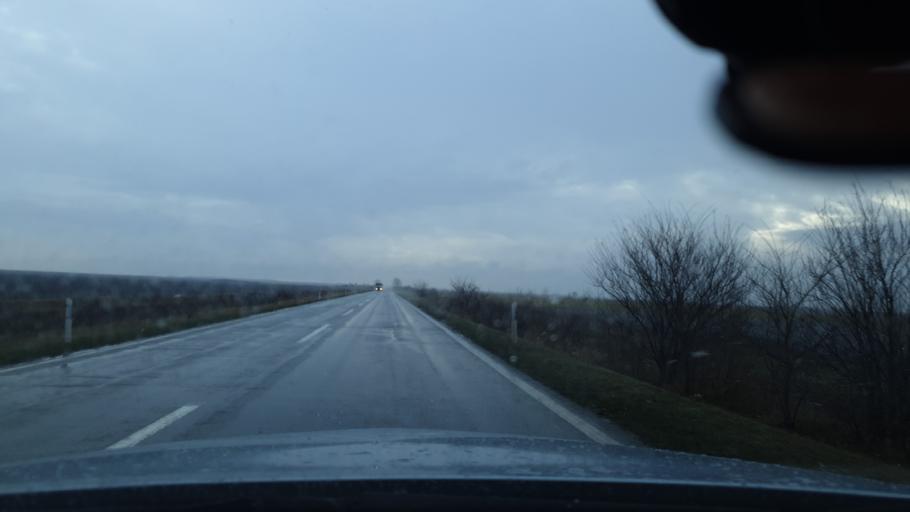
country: RS
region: Autonomna Pokrajina Vojvodina
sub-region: Juznobanatski Okrug
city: Pancevo
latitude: 44.8430
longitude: 20.7929
